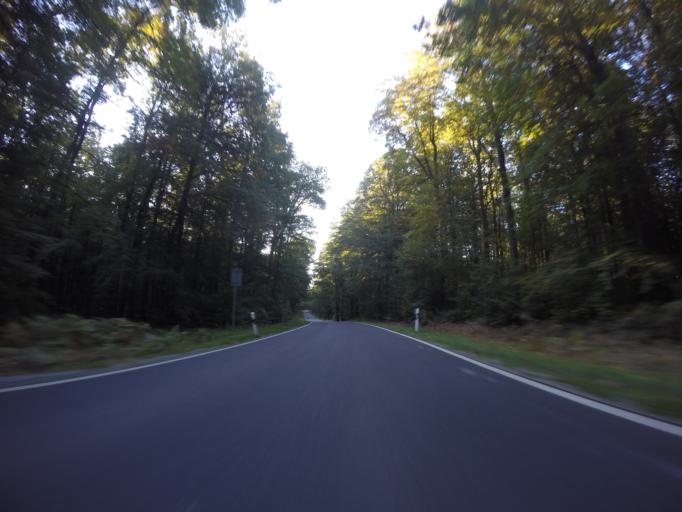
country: DE
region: Bavaria
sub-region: Regierungsbezirk Unterfranken
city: Altenbuch
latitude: 49.8758
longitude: 9.4045
